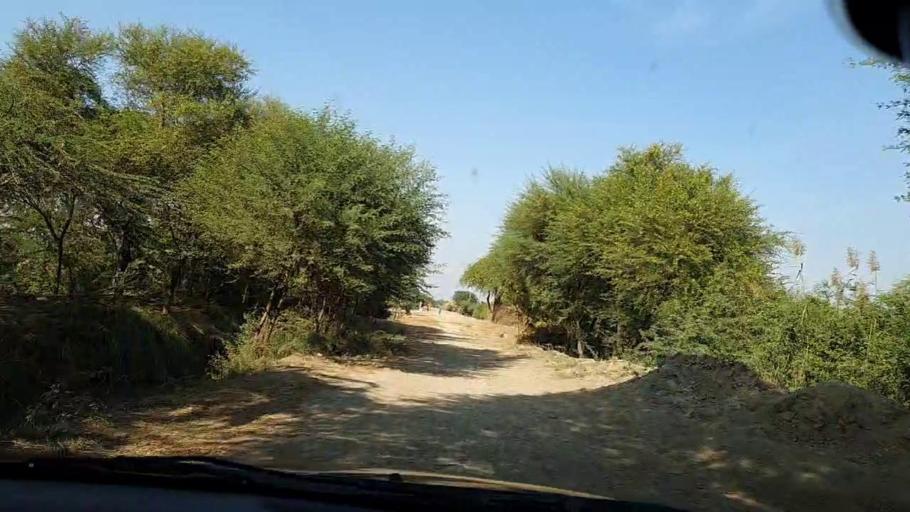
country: PK
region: Sindh
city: Mirpur Batoro
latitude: 24.6510
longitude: 68.2545
